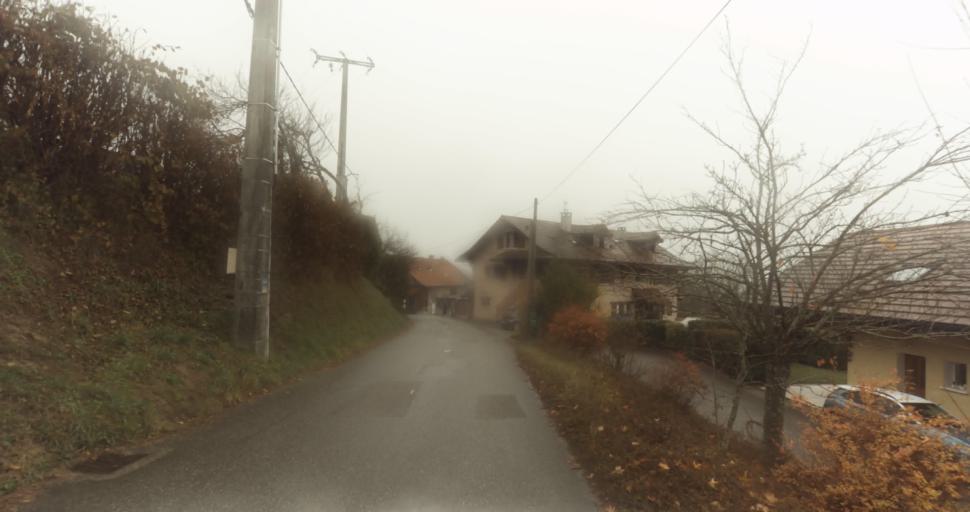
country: FR
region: Rhone-Alpes
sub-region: Departement de la Haute-Savoie
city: Villaz
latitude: 45.9727
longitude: 6.1886
